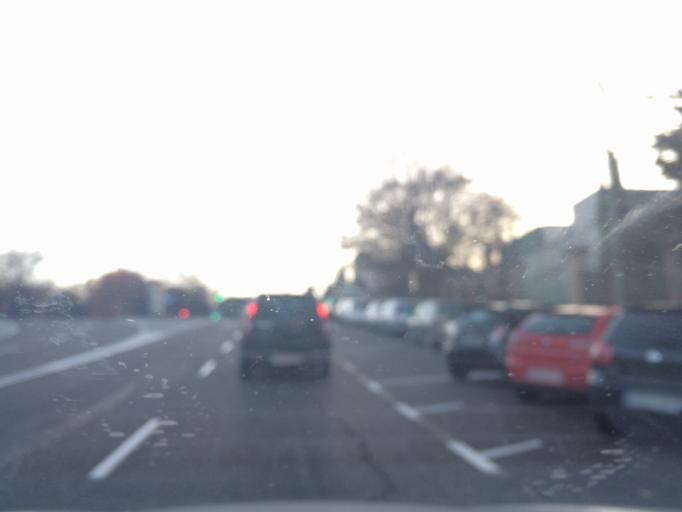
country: ES
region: Madrid
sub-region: Provincia de Madrid
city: Carabanchel
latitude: 40.4016
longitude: -3.7251
